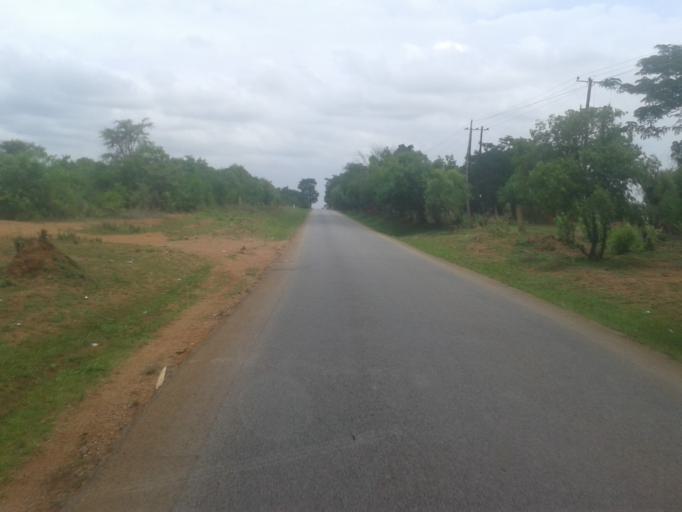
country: UG
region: Western Region
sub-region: Kiryandongo District
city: Masindi Port
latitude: 1.5090
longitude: 32.0921
